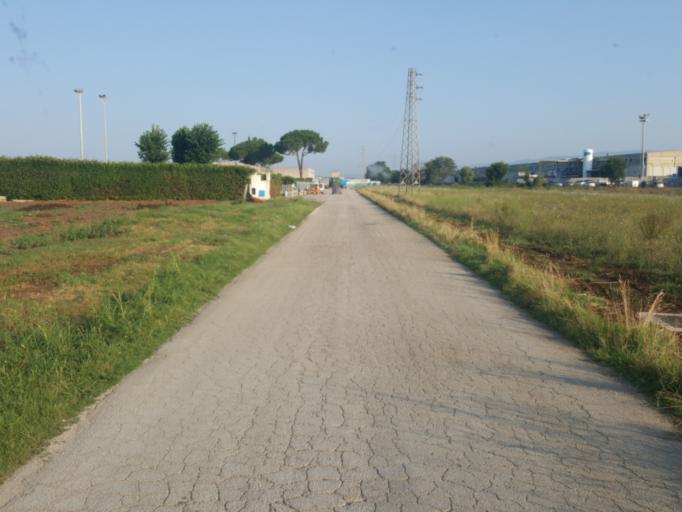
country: IT
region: Latium
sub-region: Provincia di Latina
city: Borgo Podgora
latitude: 41.5542
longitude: 12.8639
